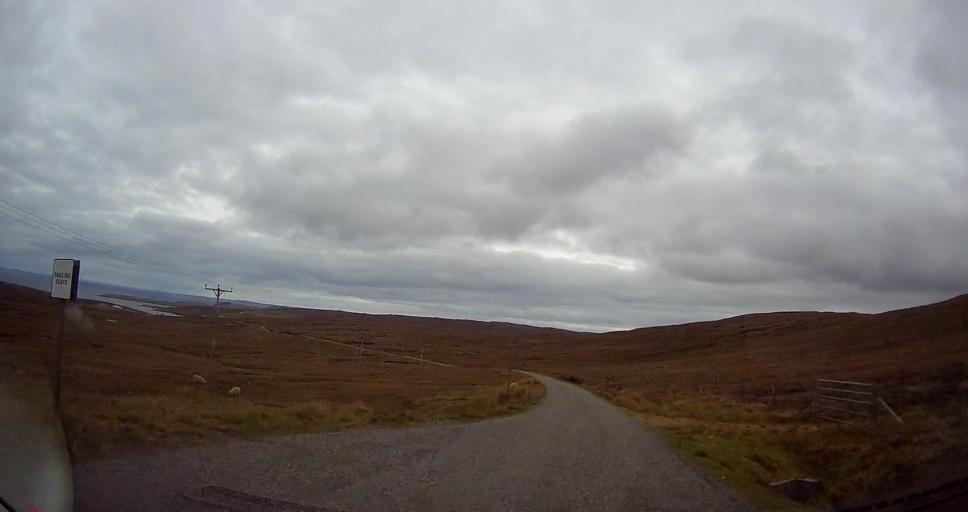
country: GB
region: Scotland
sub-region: Shetland Islands
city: Shetland
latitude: 60.5698
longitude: -1.0671
